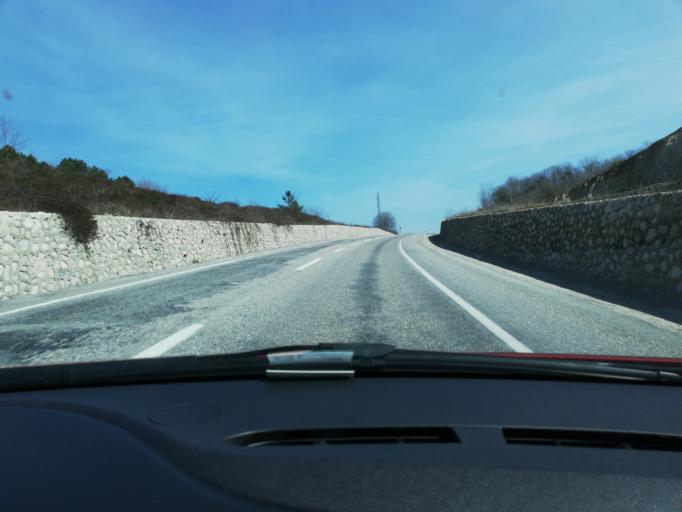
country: TR
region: Bartin
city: Amasra
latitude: 41.7289
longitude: 32.4073
